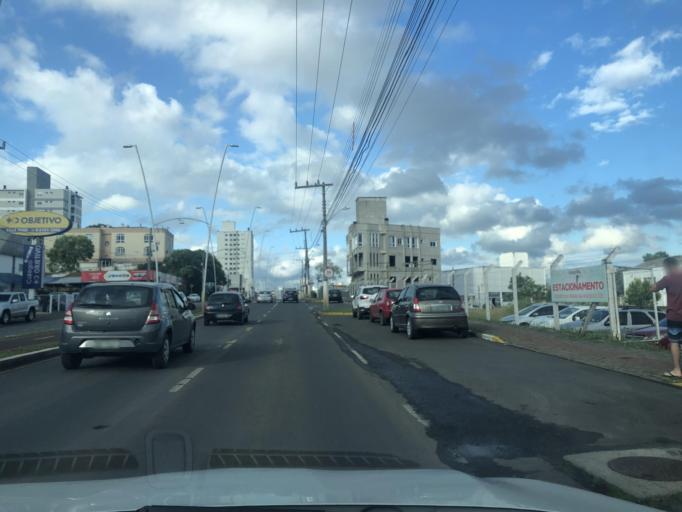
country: BR
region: Santa Catarina
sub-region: Lages
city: Lages
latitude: -27.8047
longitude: -50.3175
